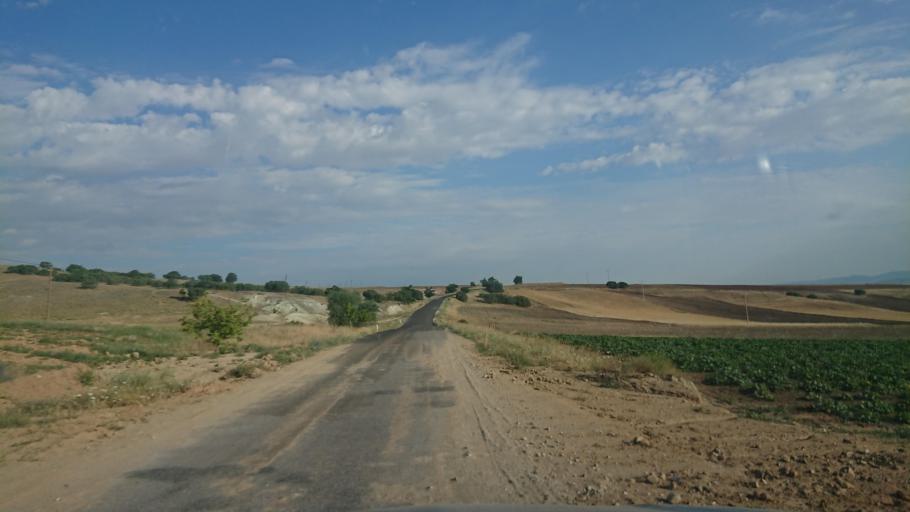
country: TR
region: Aksaray
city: Ortakoy
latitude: 38.8088
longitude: 34.0573
